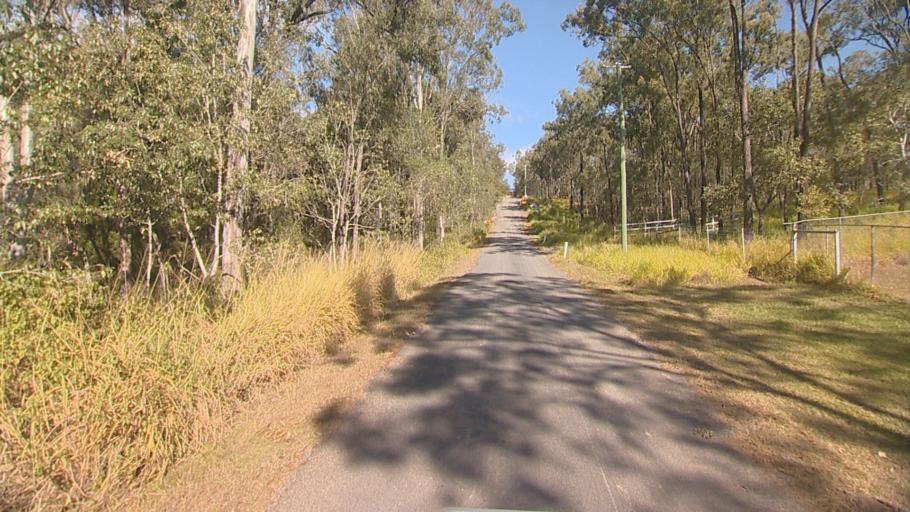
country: AU
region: Queensland
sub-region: Logan
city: Chambers Flat
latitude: -27.8105
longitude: 153.0818
